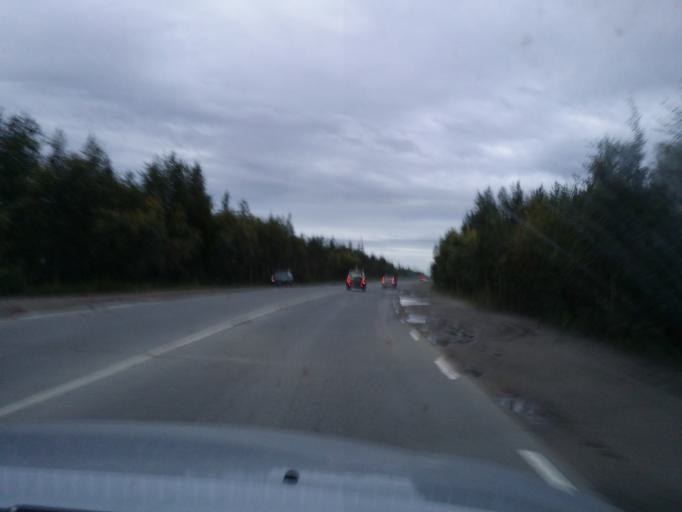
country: RU
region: Khanty-Mansiyskiy Avtonomnyy Okrug
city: Nizhnevartovsk
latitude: 60.9626
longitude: 76.6619
